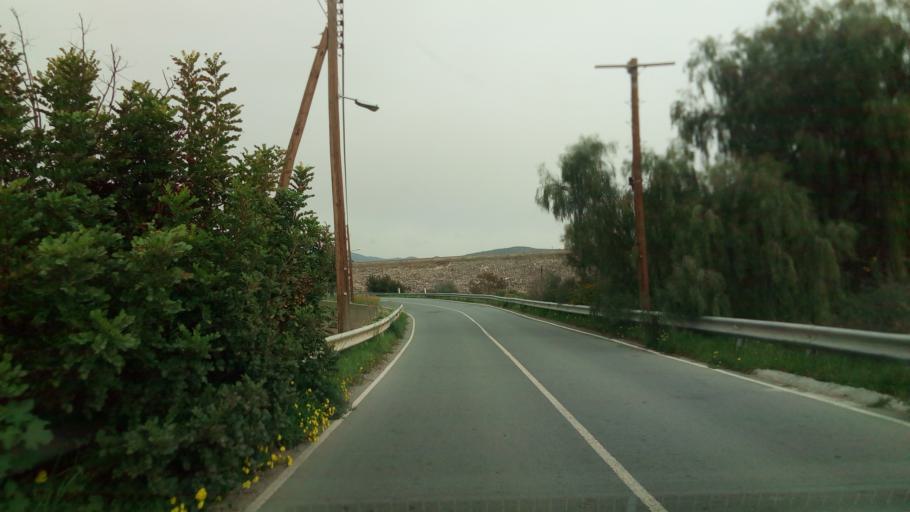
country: CY
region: Limassol
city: Mouttagiaka
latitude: 34.7410
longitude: 33.0838
